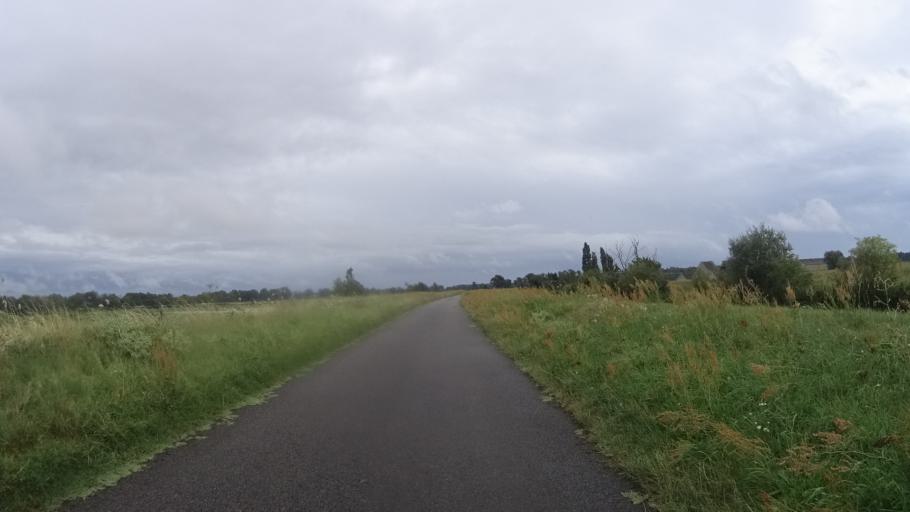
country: FR
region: Centre
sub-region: Departement du Loiret
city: Checy
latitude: 47.8820
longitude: 2.0150
